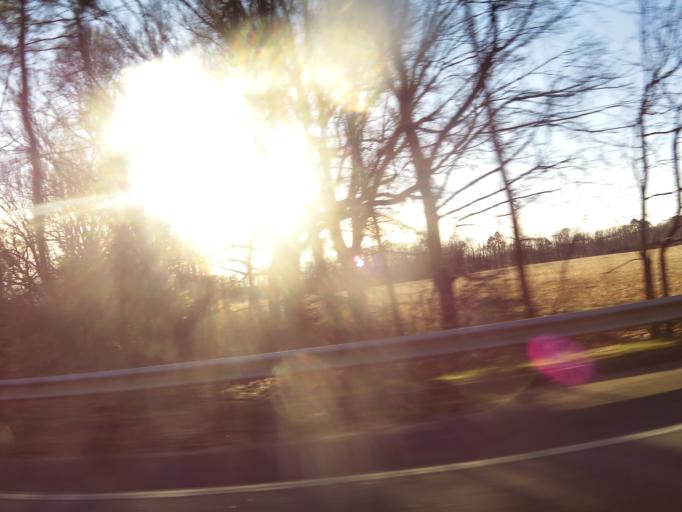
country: US
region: Virginia
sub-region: City of Franklin
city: Franklin
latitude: 36.6563
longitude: -76.8768
